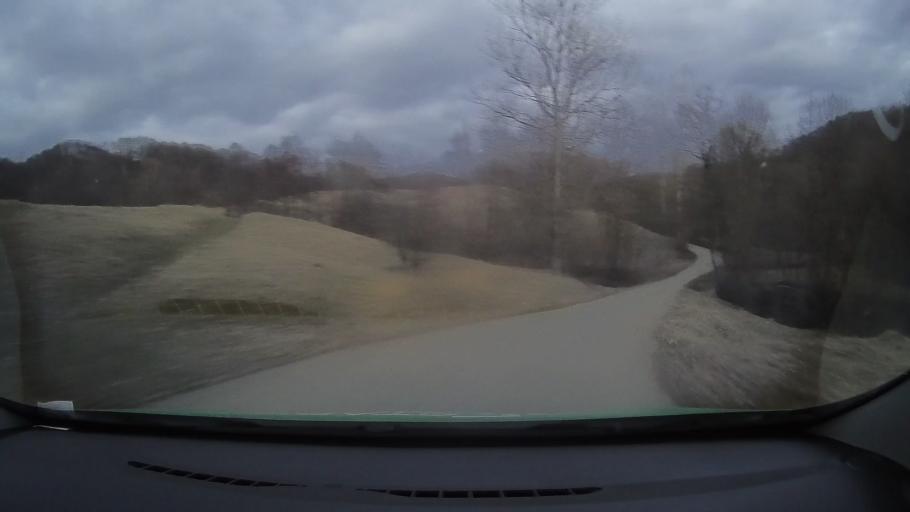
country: RO
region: Prahova
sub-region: Comuna Adunati
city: Adunati
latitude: 45.1206
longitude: 25.5979
